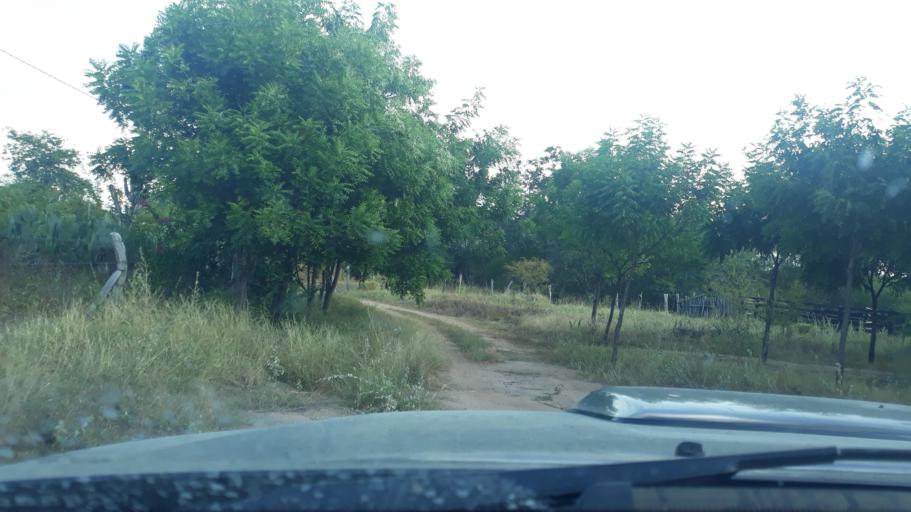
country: BR
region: Bahia
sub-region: Riacho De Santana
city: Riacho de Santana
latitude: -13.8662
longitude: -43.0778
